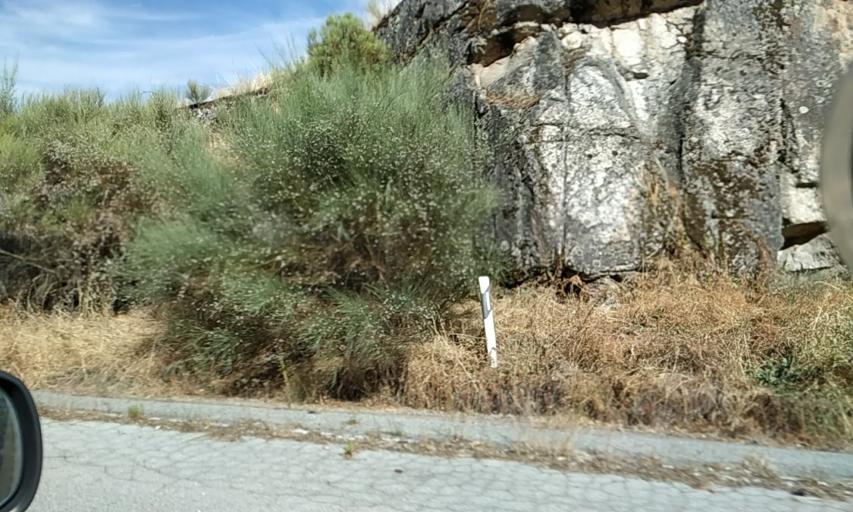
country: PT
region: Vila Real
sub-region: Sabrosa
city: Sabrosa
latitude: 41.3638
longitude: -7.5545
